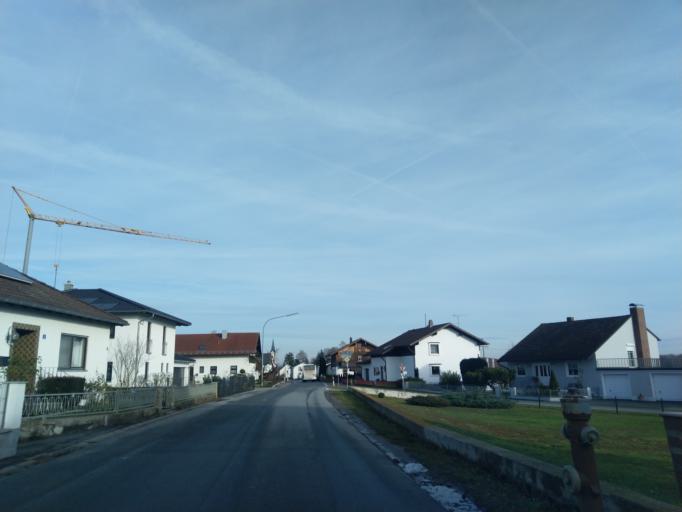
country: DE
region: Bavaria
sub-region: Lower Bavaria
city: Otzing
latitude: 48.7410
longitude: 12.8189
